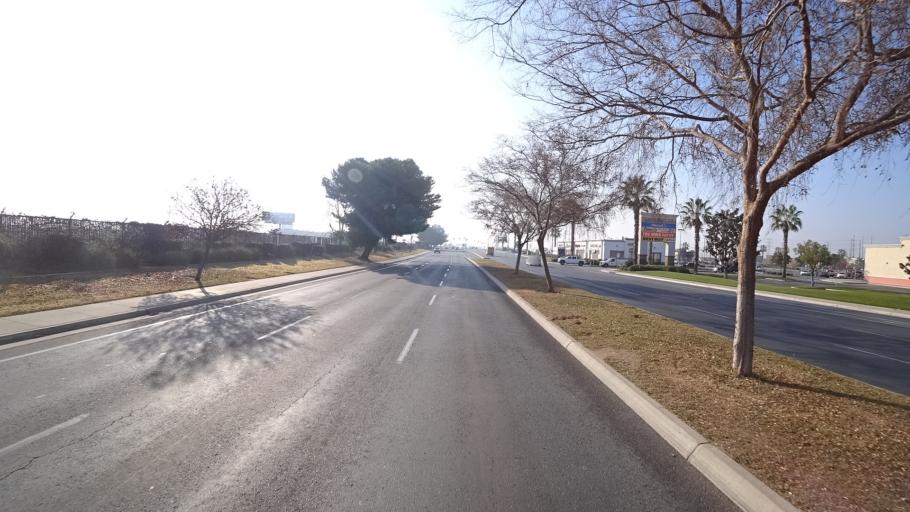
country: US
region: California
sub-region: Kern County
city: Greenacres
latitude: 35.3859
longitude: -119.0921
